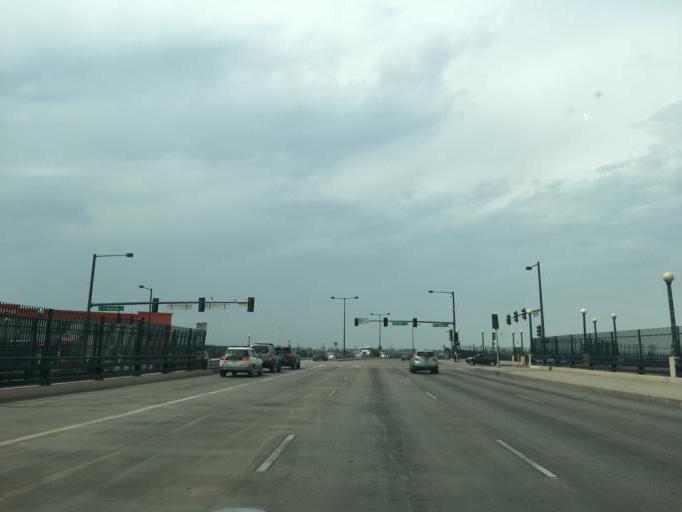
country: US
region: Colorado
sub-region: Denver County
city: Denver
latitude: 39.7588
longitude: -104.9931
